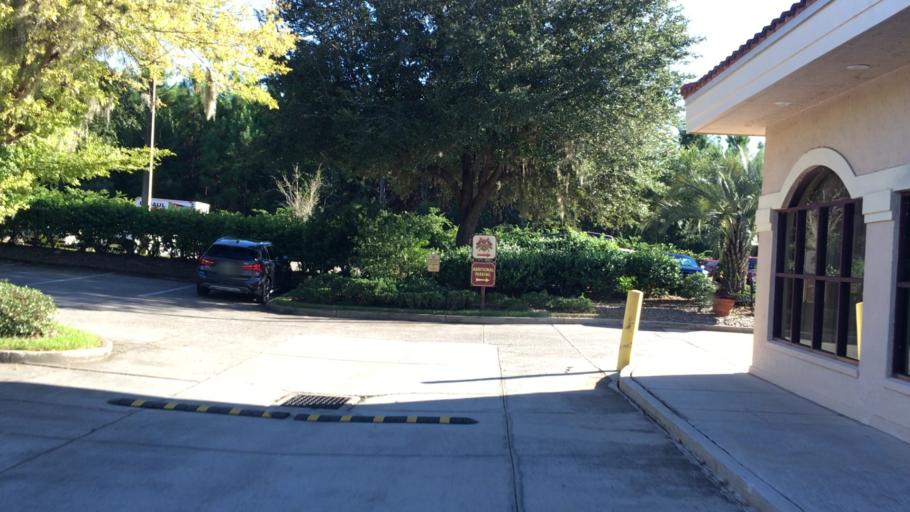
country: US
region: Florida
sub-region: Alachua County
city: Alachua
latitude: 29.6915
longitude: -82.4517
